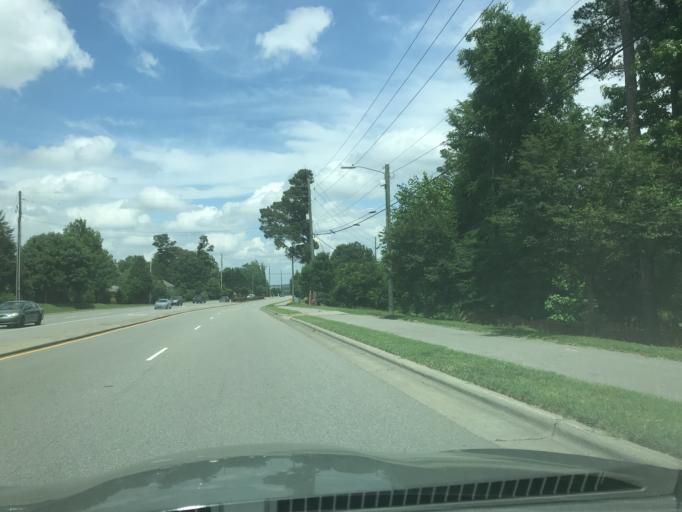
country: US
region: North Carolina
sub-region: Wake County
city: Wake Forest
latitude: 35.9304
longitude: -78.5840
